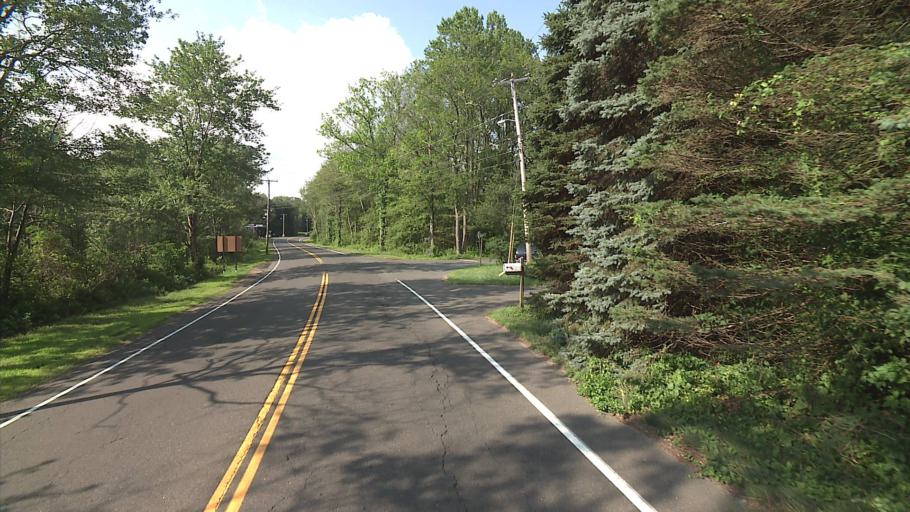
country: US
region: Connecticut
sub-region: Middlesex County
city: Higganum
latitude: 41.4307
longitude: -72.5601
